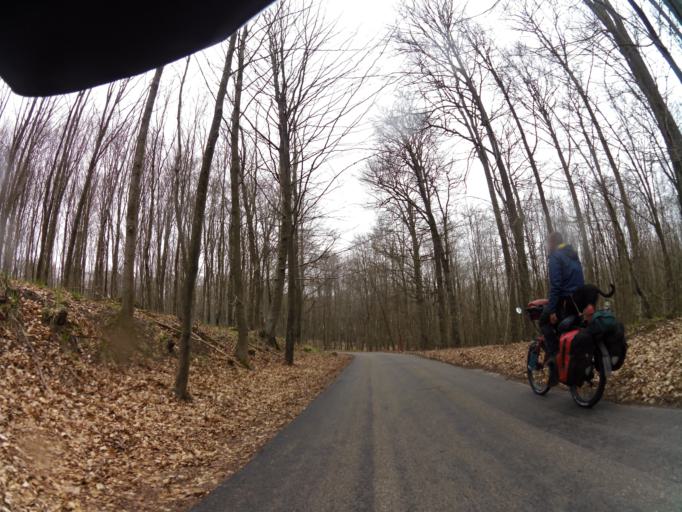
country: PL
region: West Pomeranian Voivodeship
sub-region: Powiat koszalinski
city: Bobolice
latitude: 53.9504
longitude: 16.6707
